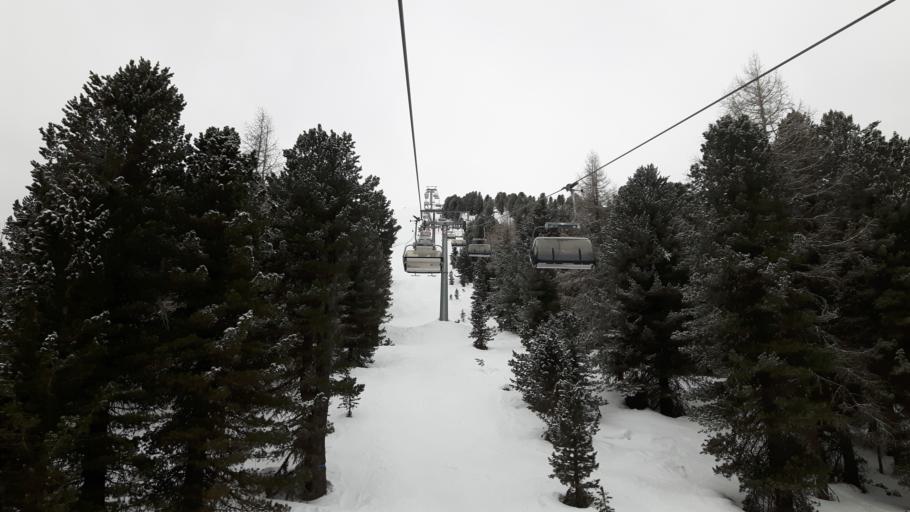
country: IT
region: Trentino-Alto Adige
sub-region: Provincia di Trento
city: Panchia
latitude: 46.3490
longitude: 11.5375
